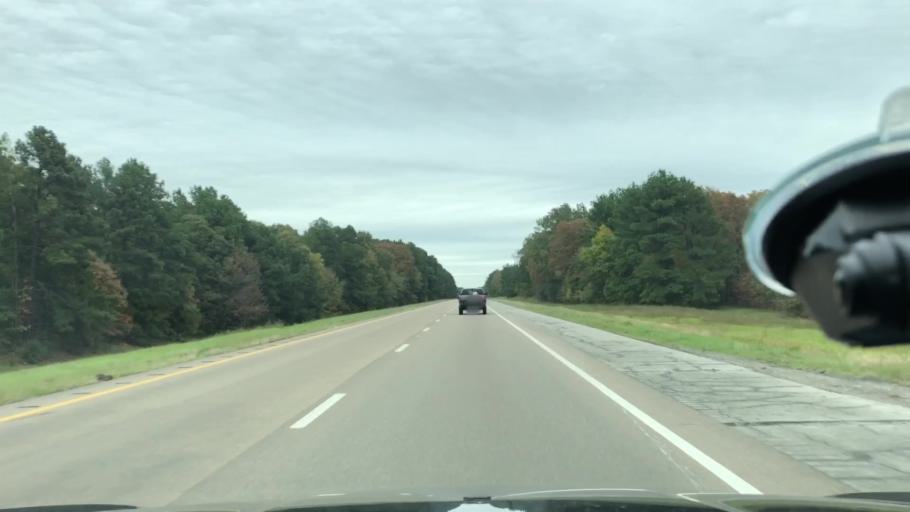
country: US
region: Texas
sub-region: Morris County
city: Naples
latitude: 33.3031
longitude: -94.7057
